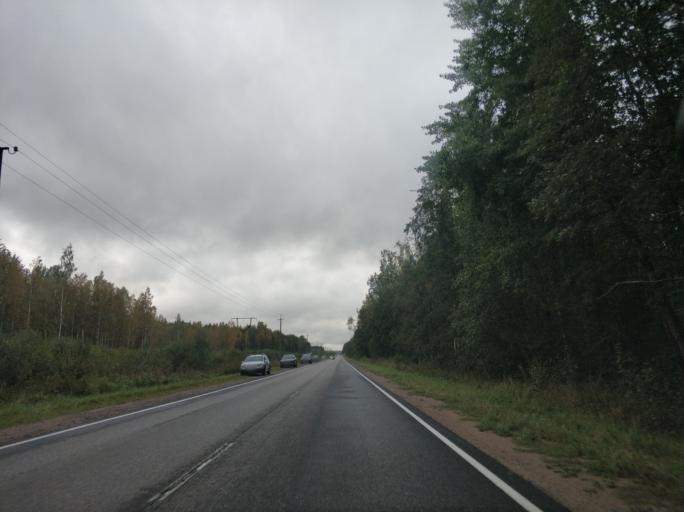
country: RU
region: Leningrad
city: Borisova Griva
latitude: 60.1058
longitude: 30.9586
